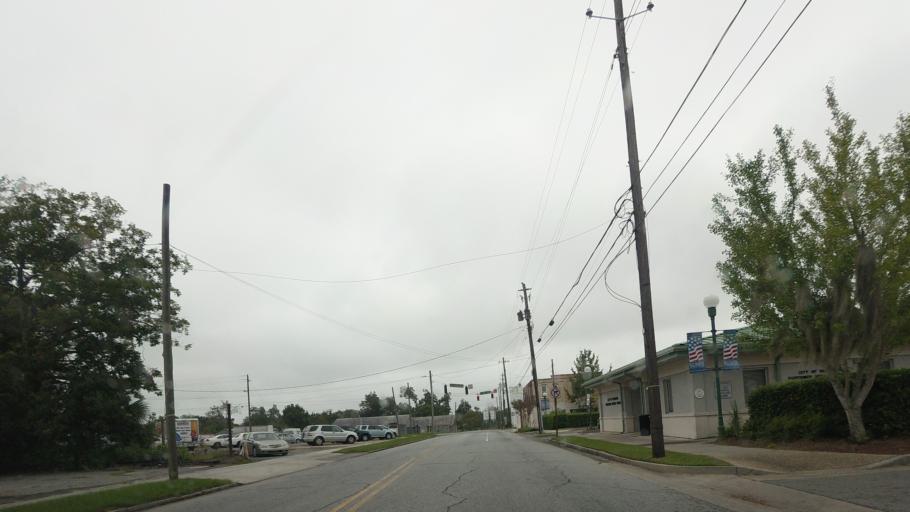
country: US
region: Georgia
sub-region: Lowndes County
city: Valdosta
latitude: 30.8322
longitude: -83.2769
